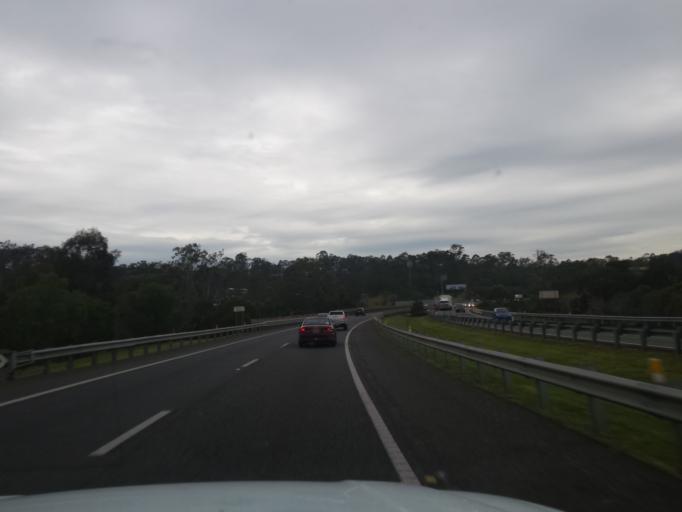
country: AU
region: Queensland
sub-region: Logan
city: Slacks Creek
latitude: -27.6666
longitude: 153.1590
